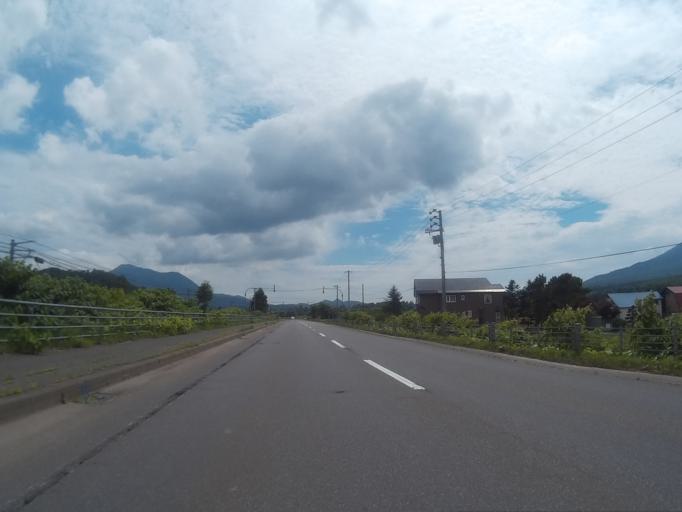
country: JP
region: Hokkaido
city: Niseko Town
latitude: 42.8508
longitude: 140.8905
